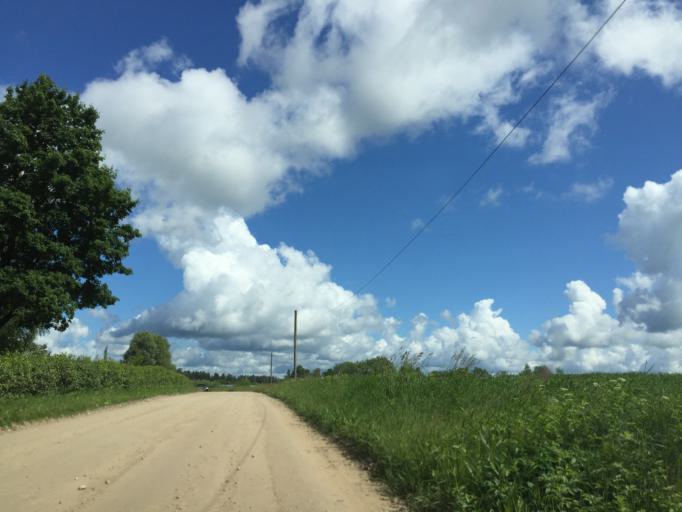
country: LV
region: Lecava
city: Iecava
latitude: 56.6205
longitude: 24.1891
